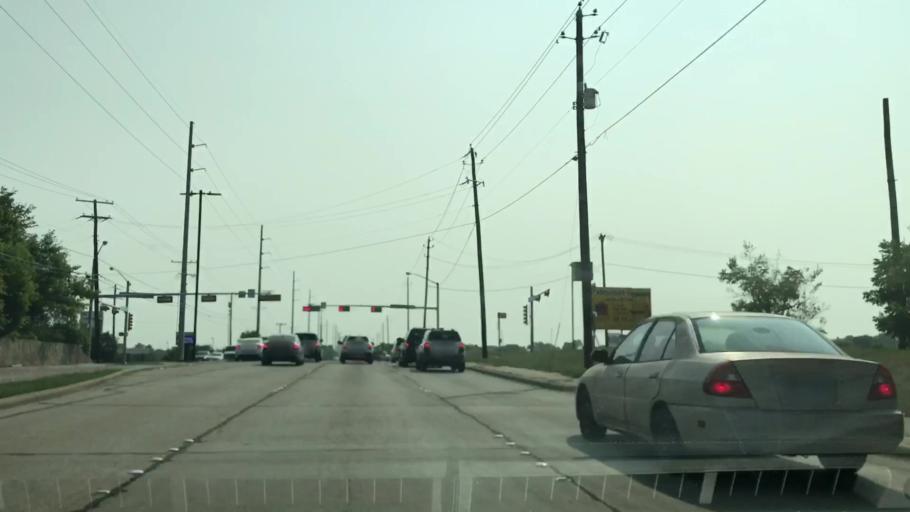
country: US
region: Texas
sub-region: Dallas County
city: Garland
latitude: 32.8874
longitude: -96.6109
